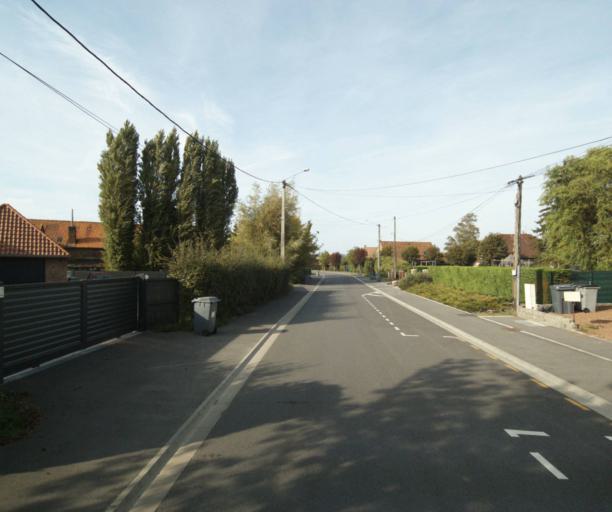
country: FR
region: Nord-Pas-de-Calais
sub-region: Departement du Nord
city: Fournes-en-Weppes
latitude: 50.5869
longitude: 2.8832
